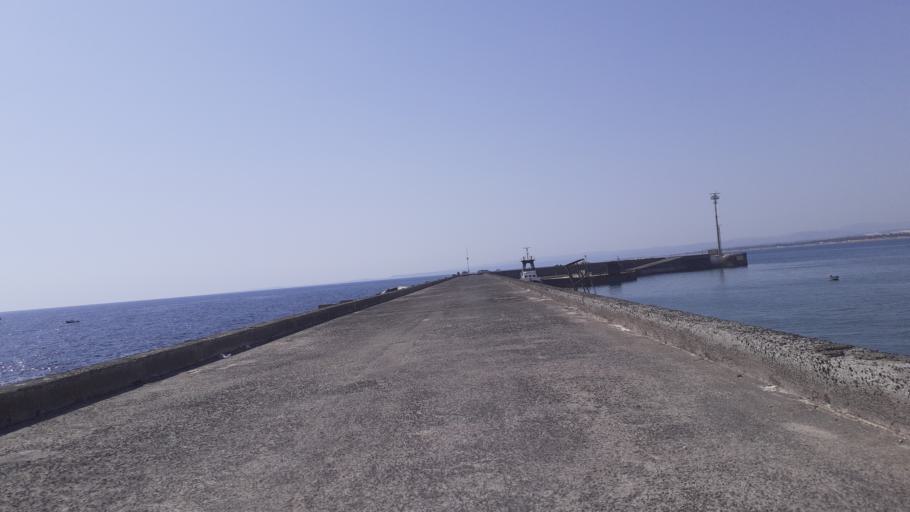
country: IT
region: Sicily
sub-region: Catania
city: Catania
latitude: 37.4906
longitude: 15.0999
